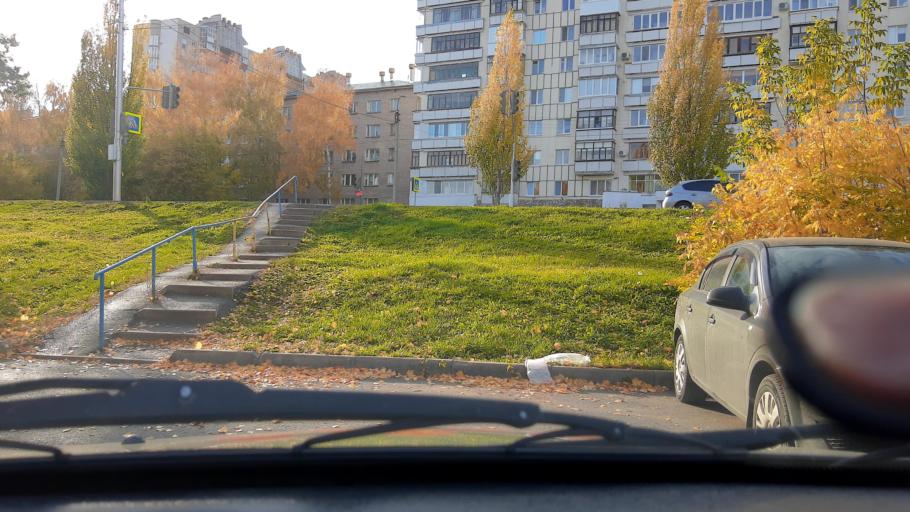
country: RU
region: Bashkortostan
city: Ufa
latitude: 54.7936
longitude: 56.0433
